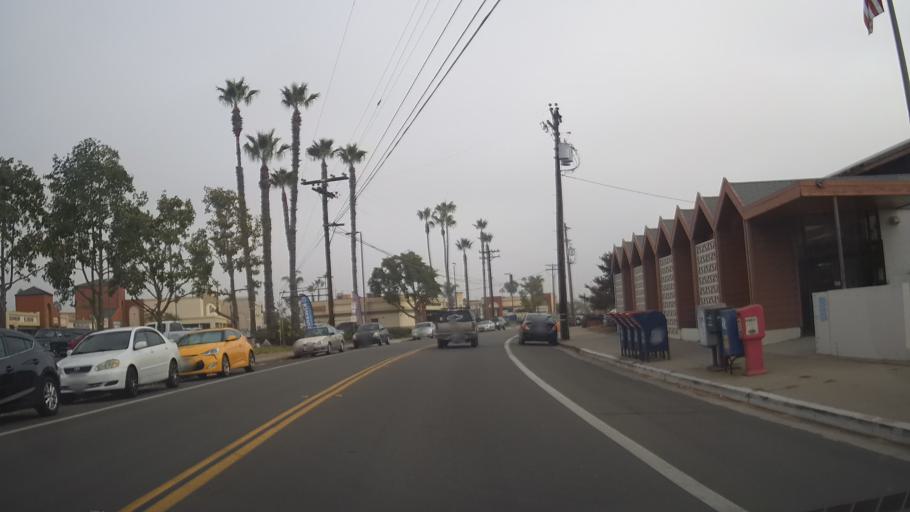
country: US
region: California
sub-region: San Diego County
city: San Diego
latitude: 32.8014
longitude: -117.1403
